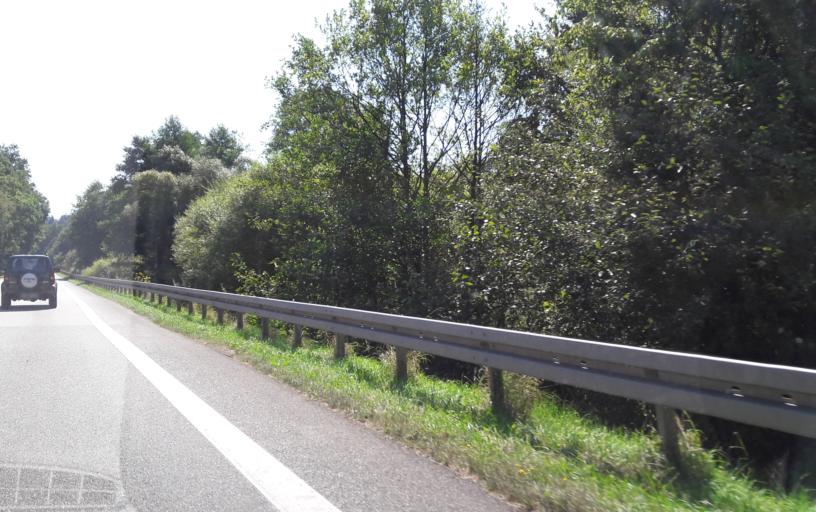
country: DE
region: Saarland
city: Nohfelden
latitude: 49.5848
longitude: 7.1259
